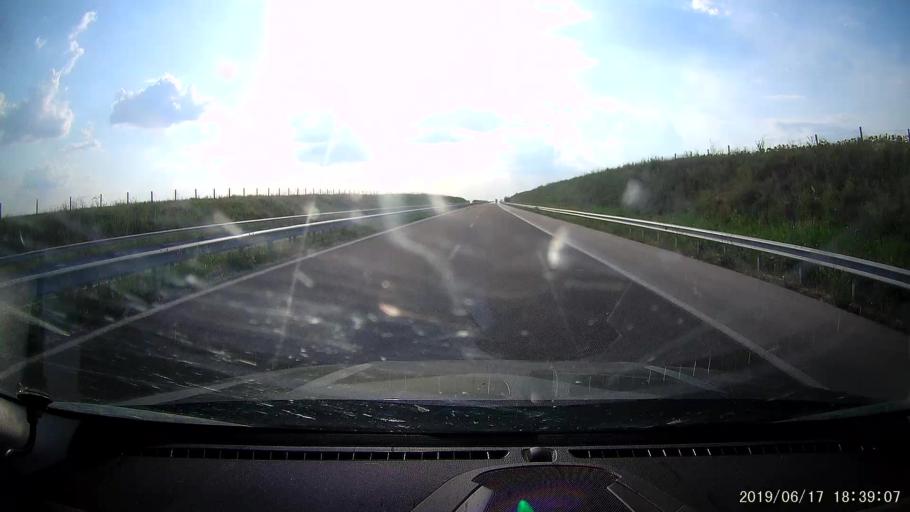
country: BG
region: Stara Zagora
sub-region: Obshtina Chirpan
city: Chirpan
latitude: 42.1422
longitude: 25.3167
